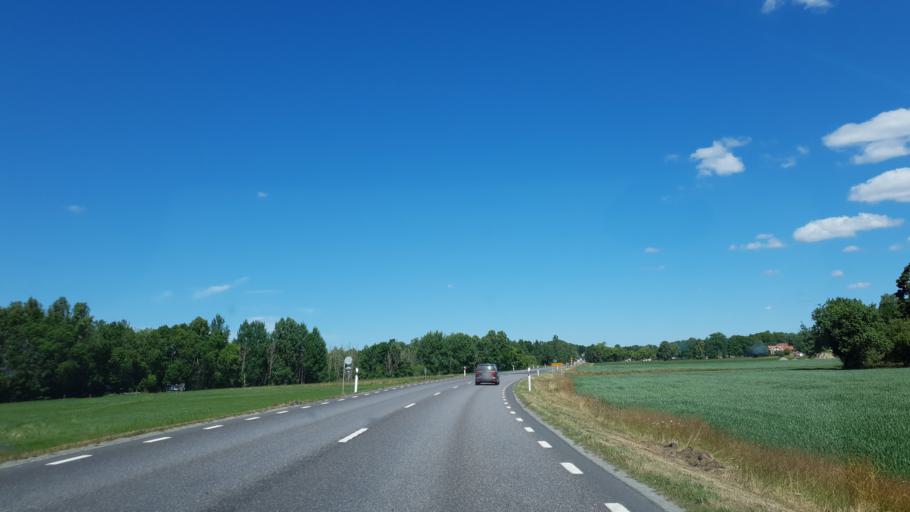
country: SE
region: Joenkoeping
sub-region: Varnamo Kommun
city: Bor
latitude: 57.0999
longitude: 14.1716
